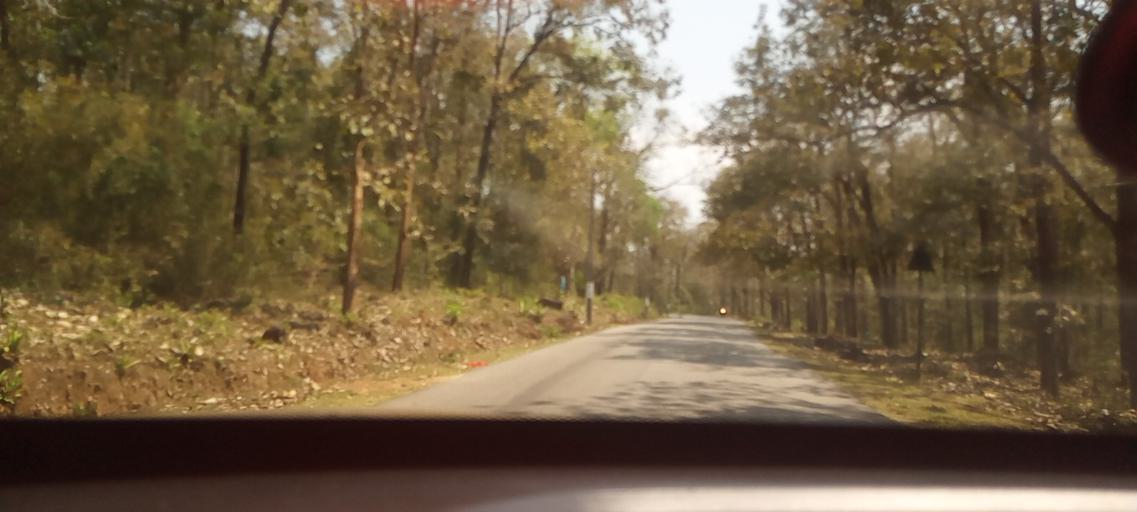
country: IN
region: Karnataka
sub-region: Chikmagalur
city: Koppa
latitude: 13.3542
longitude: 75.4951
